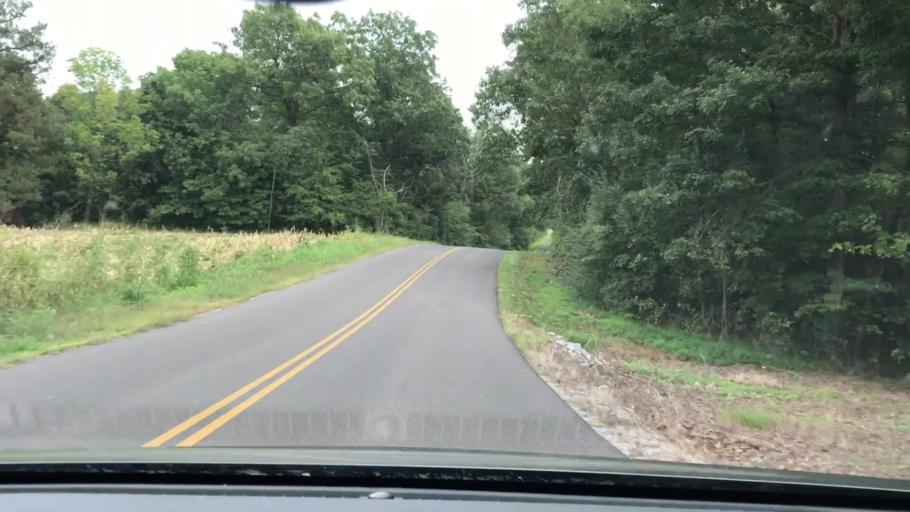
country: US
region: Kentucky
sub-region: Marshall County
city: Benton
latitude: 36.8317
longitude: -88.3614
